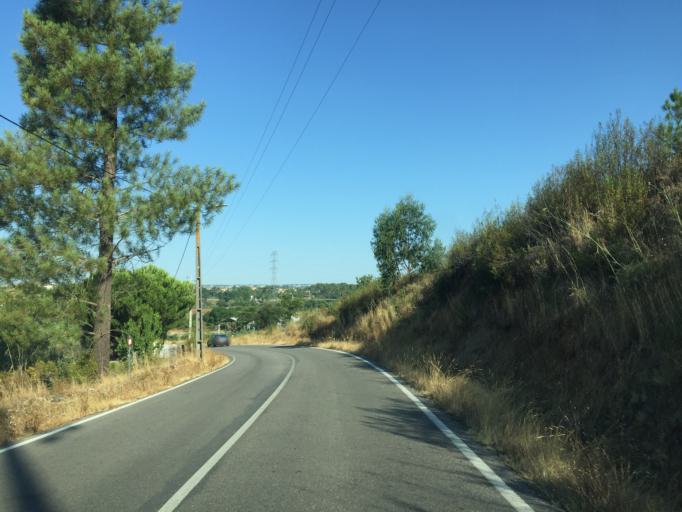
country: PT
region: Santarem
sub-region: Tomar
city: Tomar
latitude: 39.5915
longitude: -8.3564
